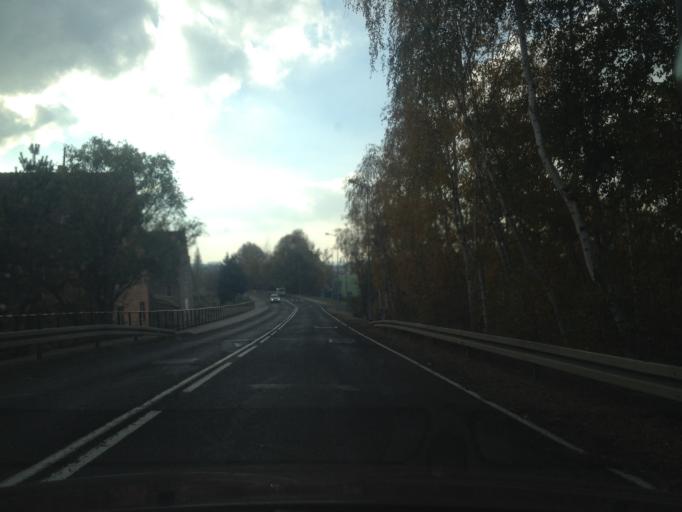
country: PL
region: Lower Silesian Voivodeship
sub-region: Powiat zgorzelecki
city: Zgorzelec
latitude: 51.1413
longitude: 15.0193
